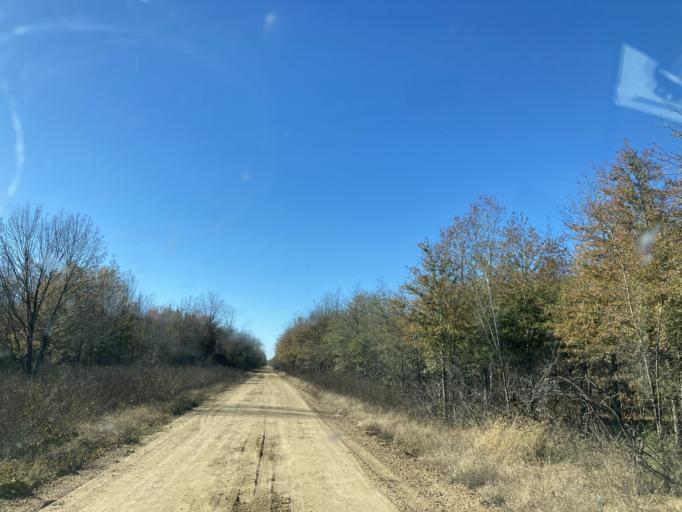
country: US
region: Mississippi
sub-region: Sharkey County
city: Rolling Fork
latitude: 32.7491
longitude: -90.6637
